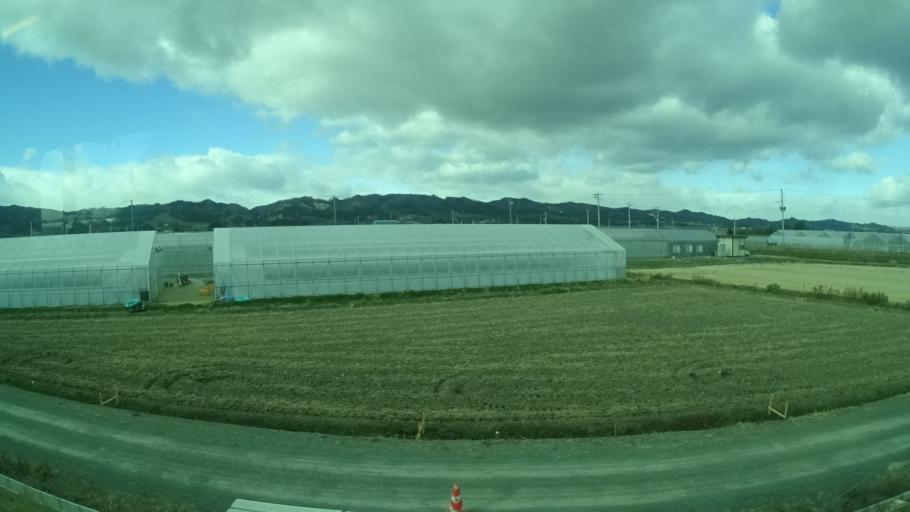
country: JP
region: Miyagi
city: Watari
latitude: 37.9857
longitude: 140.8900
